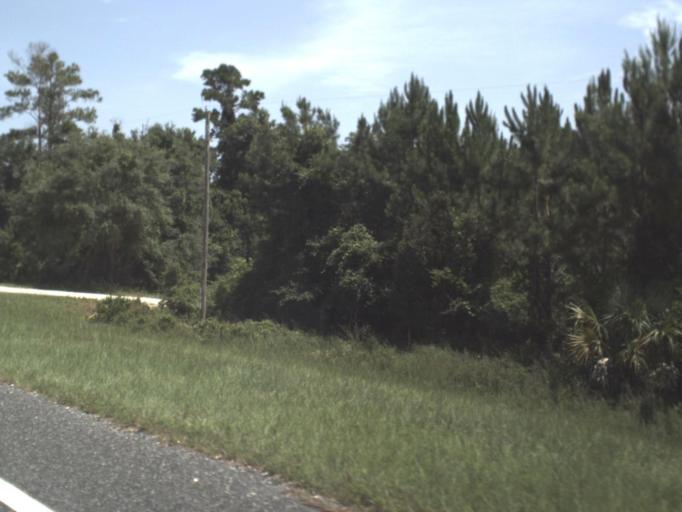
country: US
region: Florida
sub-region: Taylor County
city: Steinhatchee
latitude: 29.7736
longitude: -83.3234
